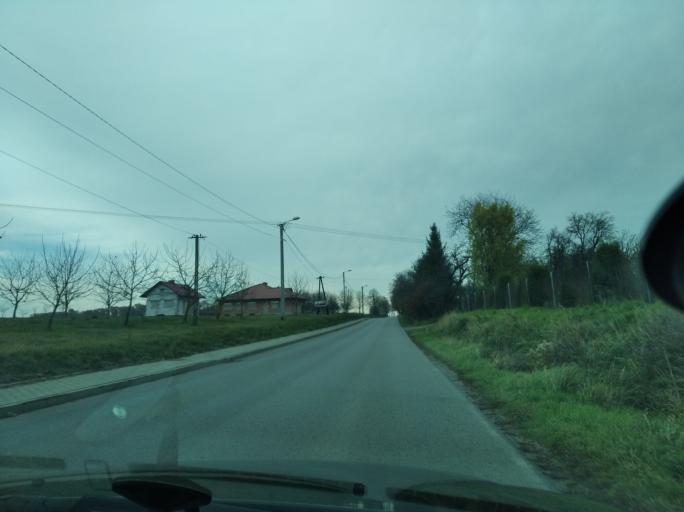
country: PL
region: Subcarpathian Voivodeship
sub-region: Powiat lancucki
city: Albigowa
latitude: 50.0317
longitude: 22.2388
